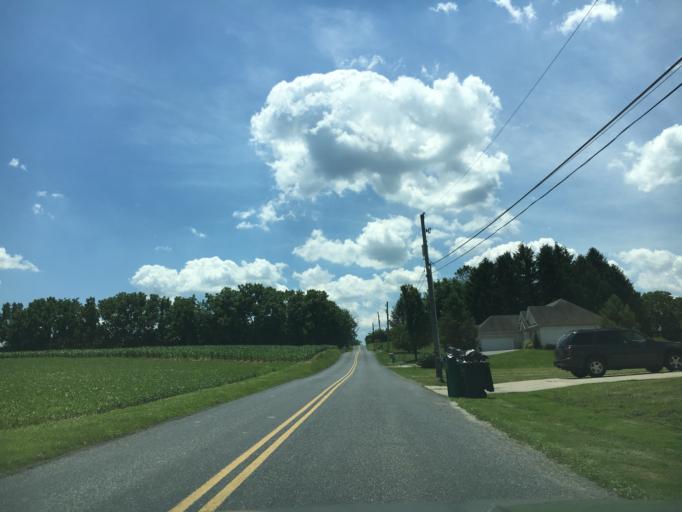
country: US
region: Pennsylvania
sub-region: Lehigh County
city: Schnecksville
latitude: 40.6637
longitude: -75.5756
